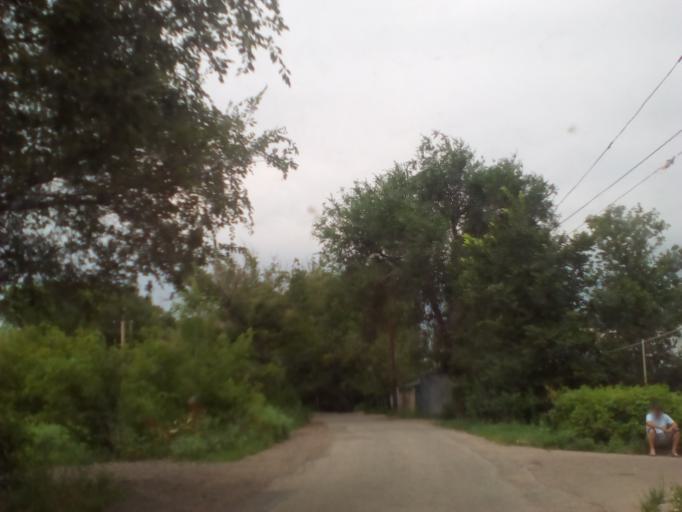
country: KZ
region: Almaty Oblysy
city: Burunday
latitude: 43.1594
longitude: 76.3892
